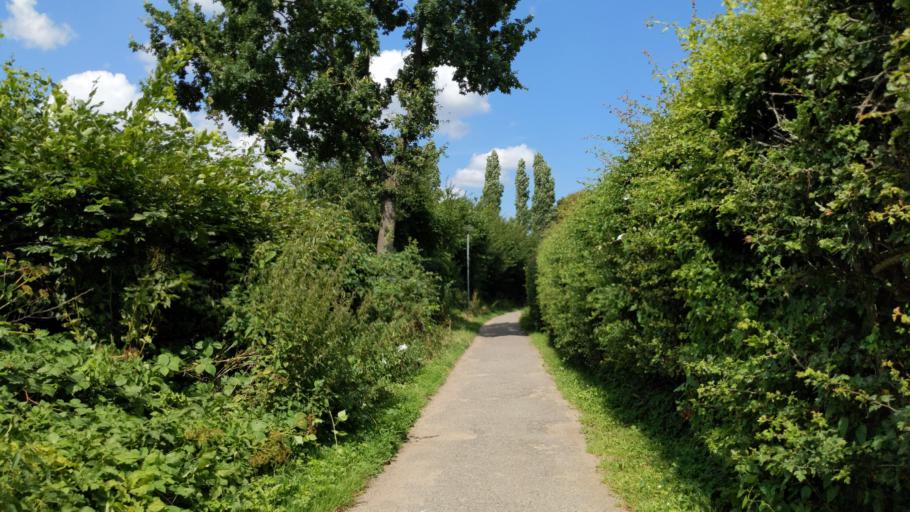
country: DE
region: Mecklenburg-Vorpommern
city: Selmsdorf
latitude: 53.9087
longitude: 10.8120
